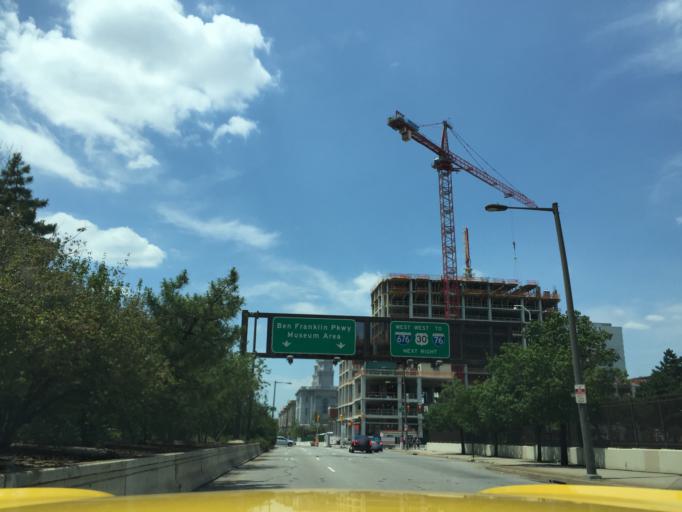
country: US
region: Pennsylvania
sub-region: Philadelphia County
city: Philadelphia
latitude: 39.9583
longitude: -75.1645
